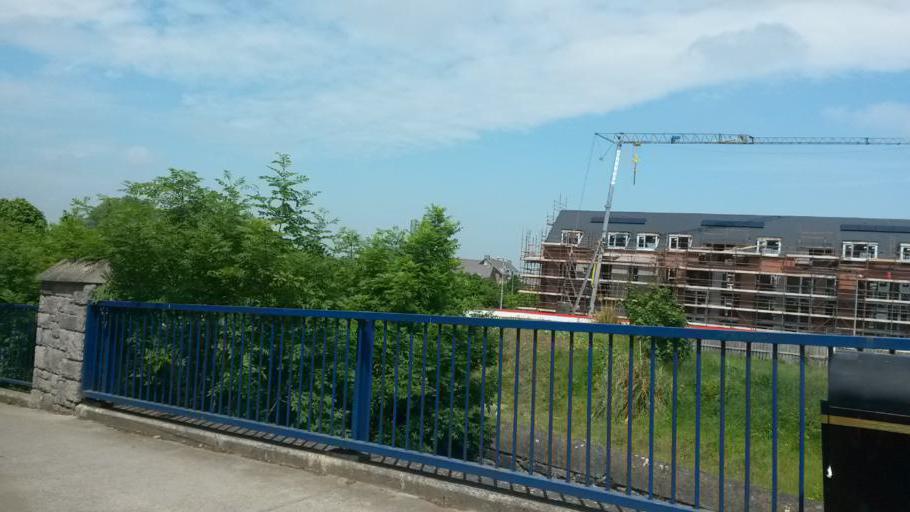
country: IE
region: Leinster
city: Donabate
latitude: 53.4855
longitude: -6.1522
